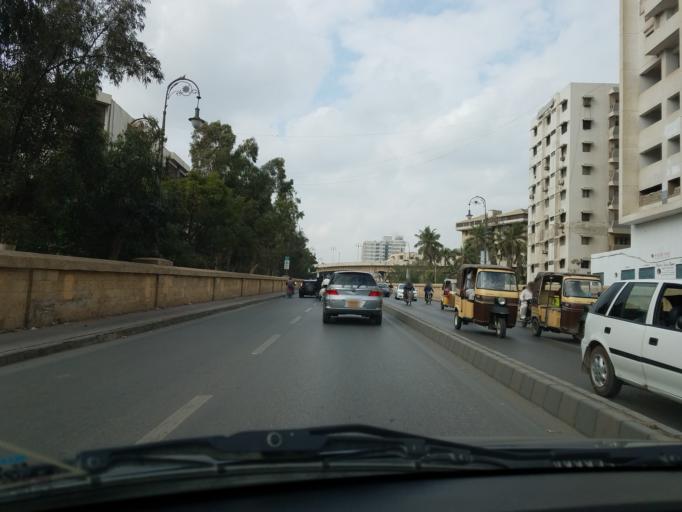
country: PK
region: Sindh
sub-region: Karachi District
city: Karachi
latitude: 24.8387
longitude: 67.0329
